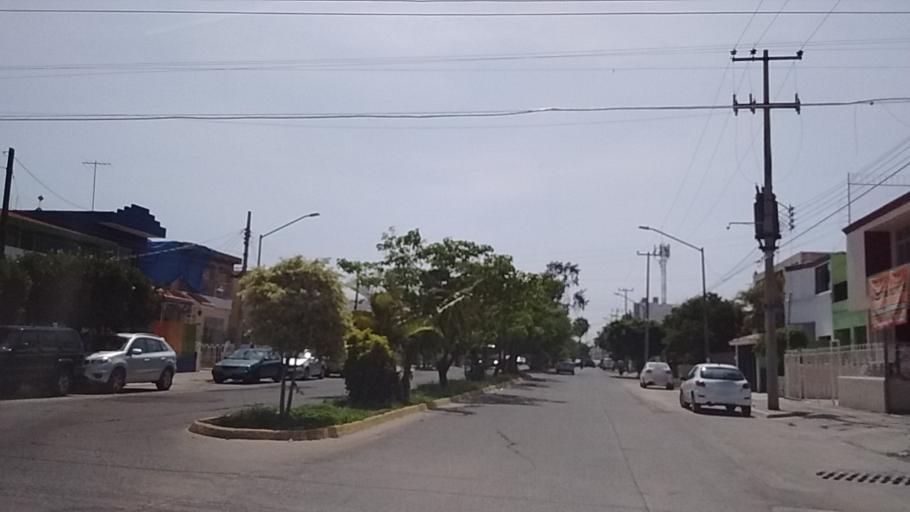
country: MX
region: Jalisco
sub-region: Zapopan
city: Zapopan
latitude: 20.6929
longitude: -103.3463
